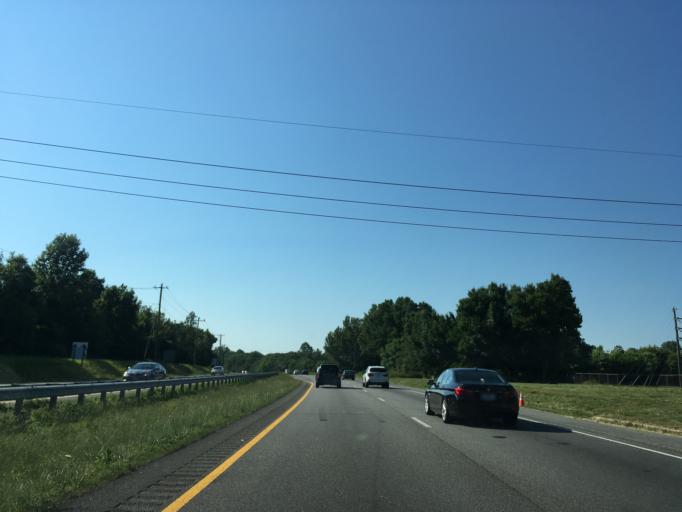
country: US
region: Maryland
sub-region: Queen Anne's County
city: Centreville
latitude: 38.9457
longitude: -76.0636
